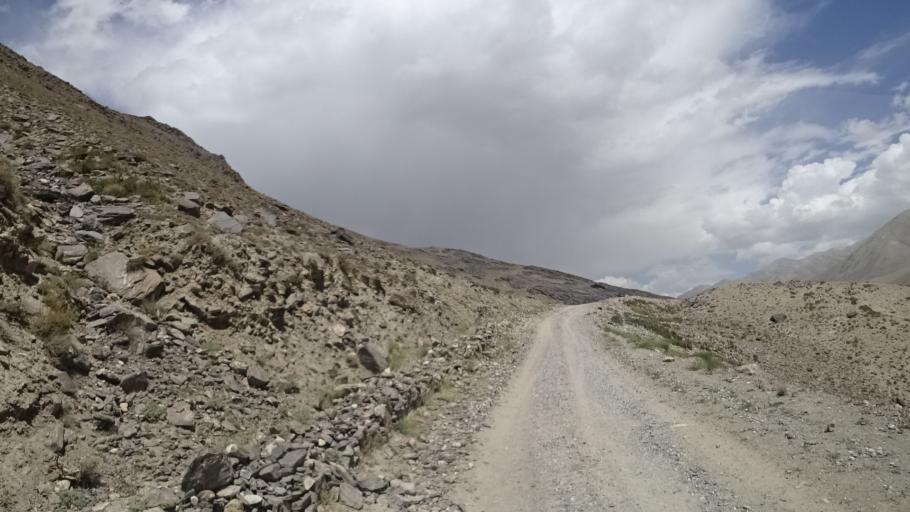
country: AF
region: Badakhshan
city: Khandud
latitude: 37.0930
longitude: 72.7061
